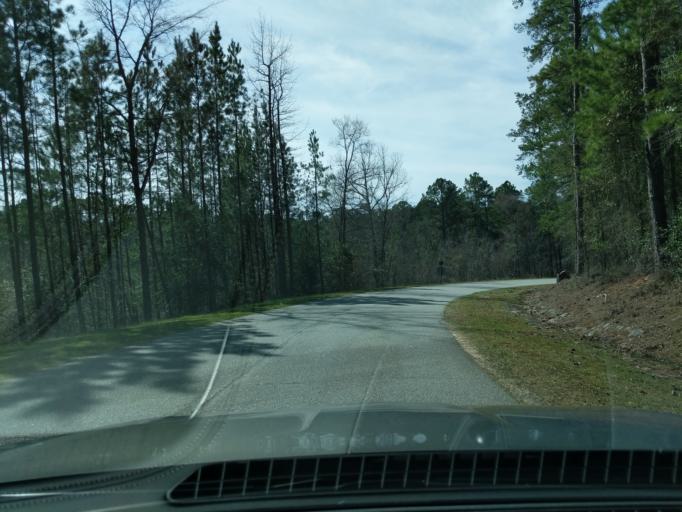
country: US
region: Georgia
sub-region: Columbia County
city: Evans
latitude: 33.6631
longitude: -82.1874
